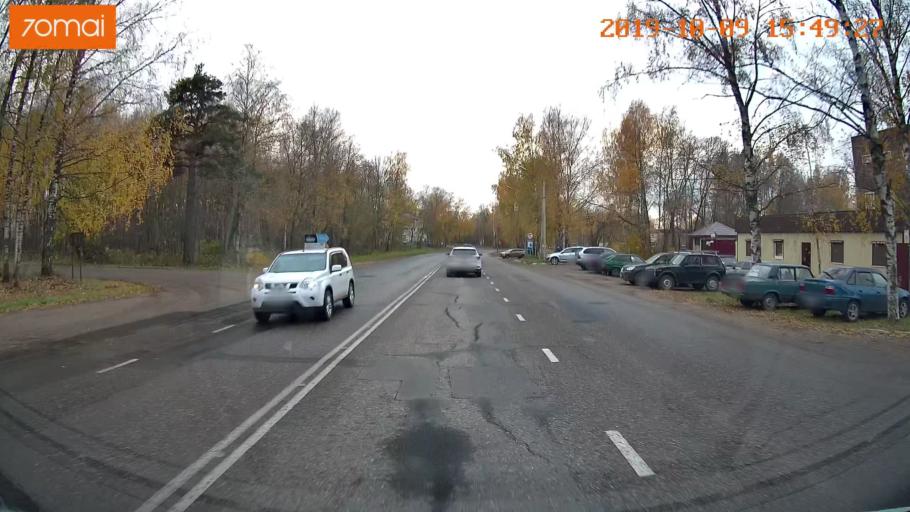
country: RU
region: Kostroma
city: Oktyabr'skiy
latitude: 57.8050
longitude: 41.0046
